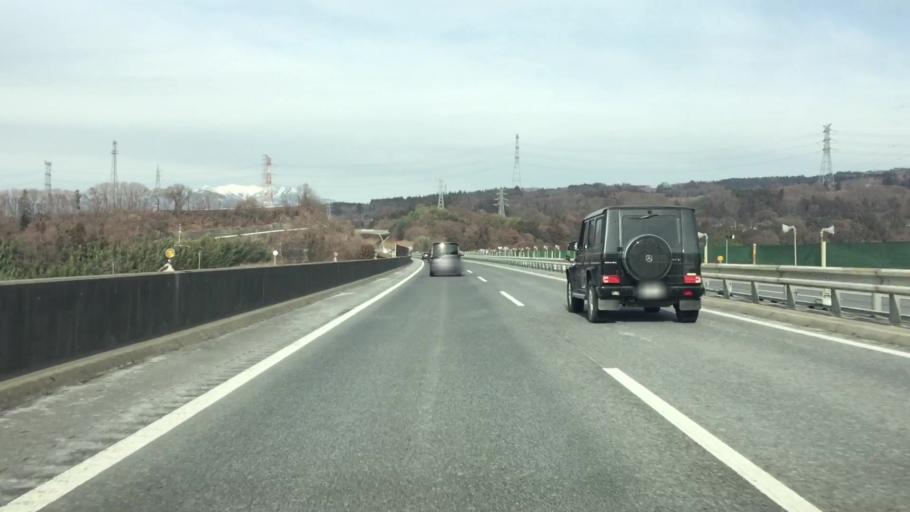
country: JP
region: Gunma
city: Numata
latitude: 36.5588
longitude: 139.0590
